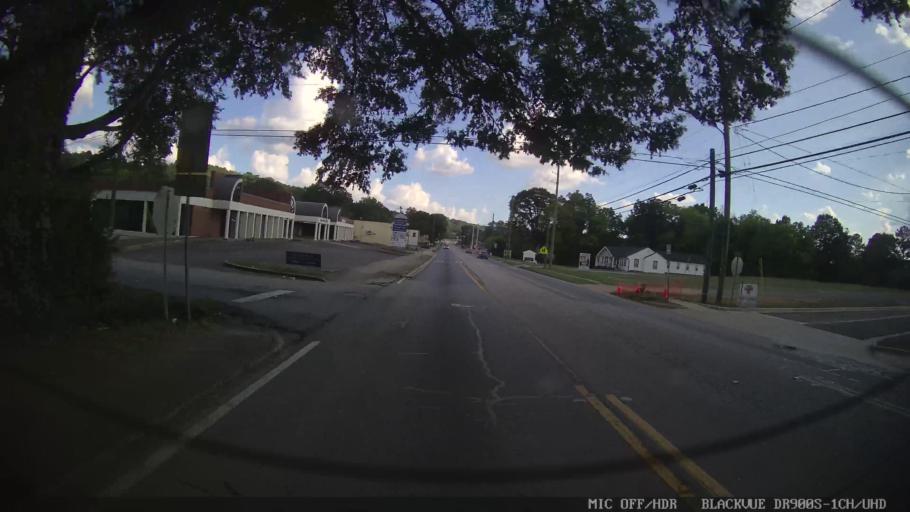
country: US
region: Georgia
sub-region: Floyd County
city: Rome
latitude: 34.2351
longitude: -85.1597
